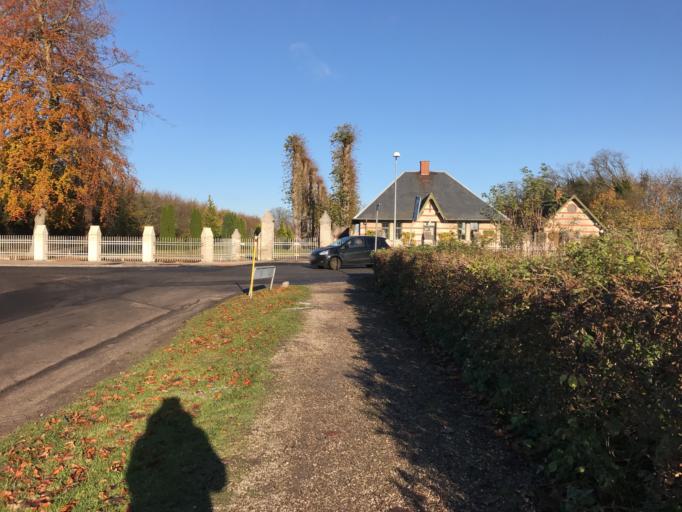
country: DK
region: Zealand
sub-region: Stevns Kommune
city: Store Heddinge
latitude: 55.3142
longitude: 12.3921
